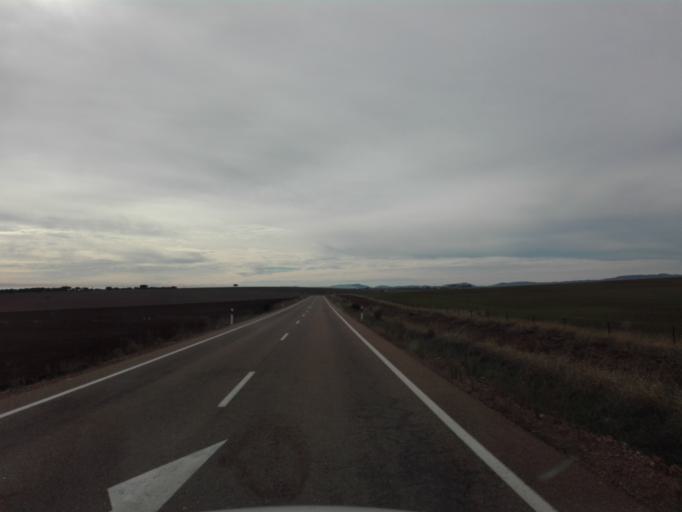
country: ES
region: Extremadura
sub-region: Provincia de Badajoz
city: Valencia de las Torres
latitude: 38.3447
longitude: -5.9656
